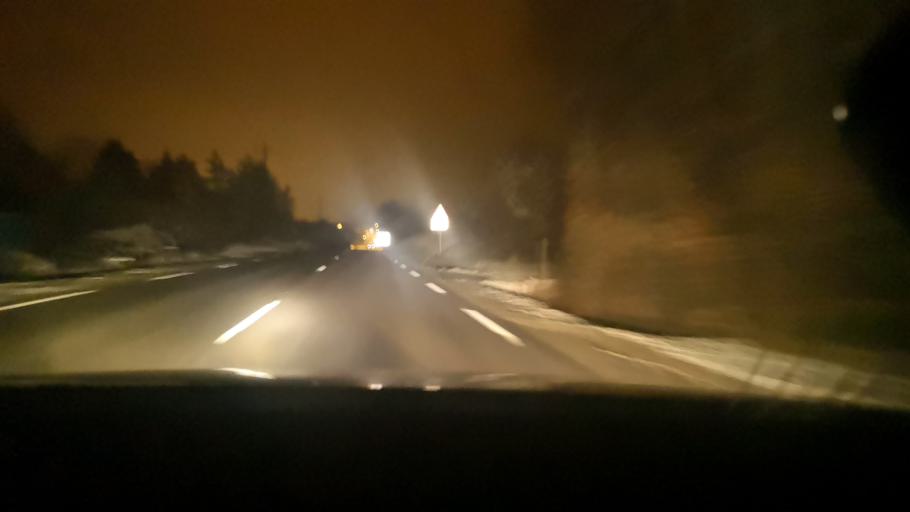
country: FR
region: Rhone-Alpes
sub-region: Departement de l'Ain
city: Ceyzeriat
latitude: 46.1744
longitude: 5.3344
